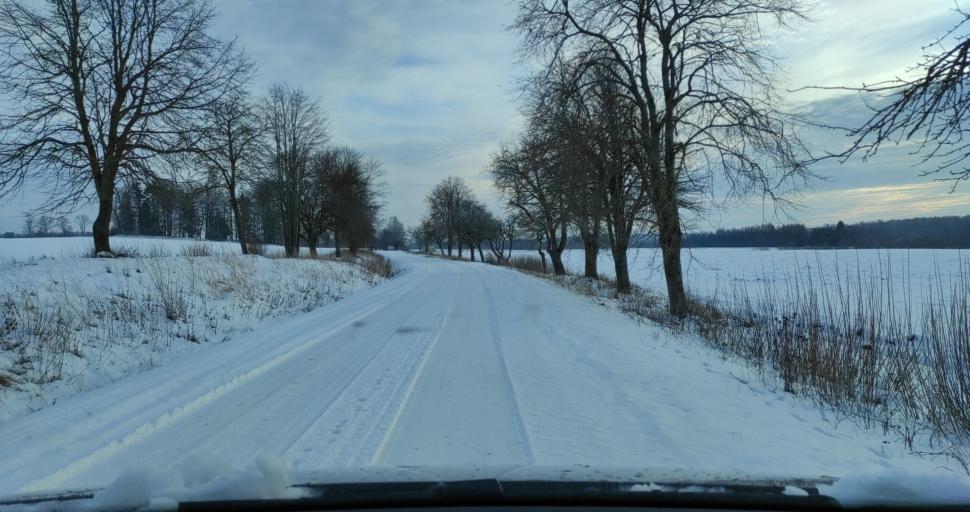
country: LV
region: Kuldigas Rajons
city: Kuldiga
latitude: 56.9511
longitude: 22.0181
